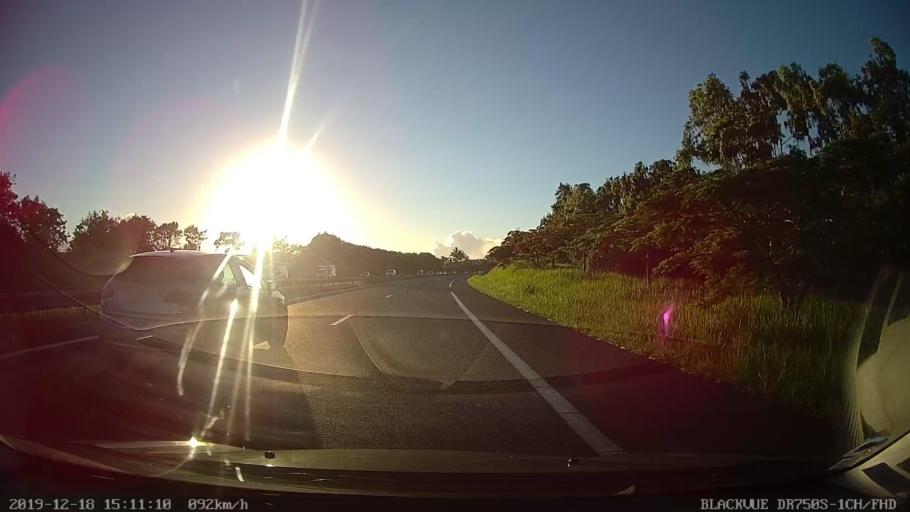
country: RE
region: Reunion
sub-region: Reunion
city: Sainte-Suzanne
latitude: -20.9039
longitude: 55.5975
